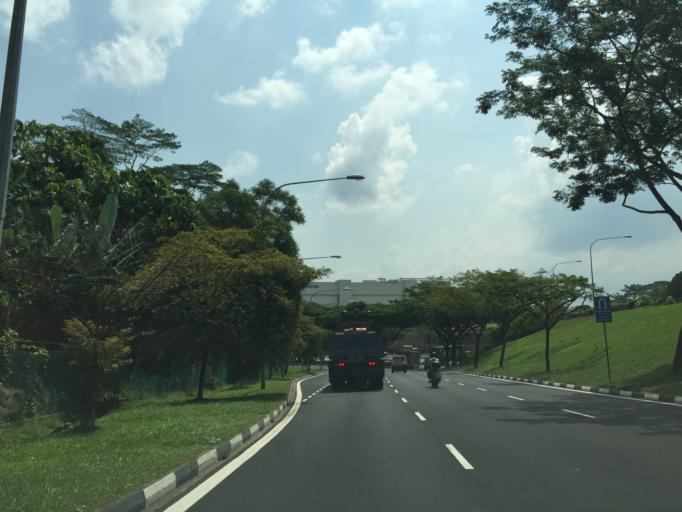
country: MY
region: Johor
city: Johor Bahru
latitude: 1.4299
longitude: 103.7691
